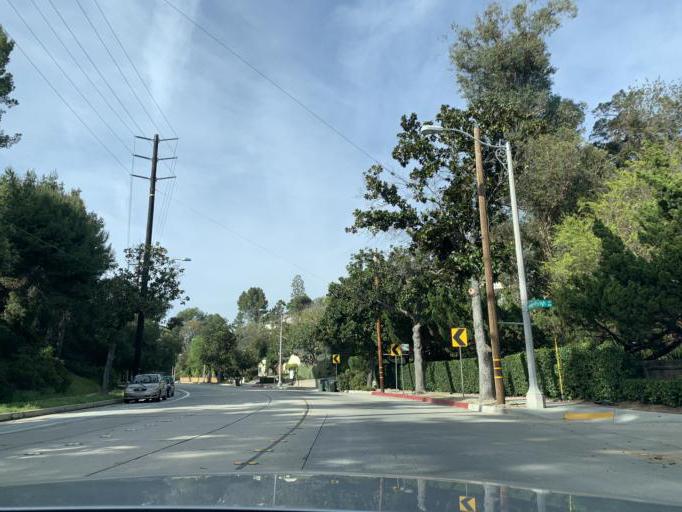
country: US
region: California
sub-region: Los Angeles County
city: South Pasadena
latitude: 34.1273
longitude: -118.1764
